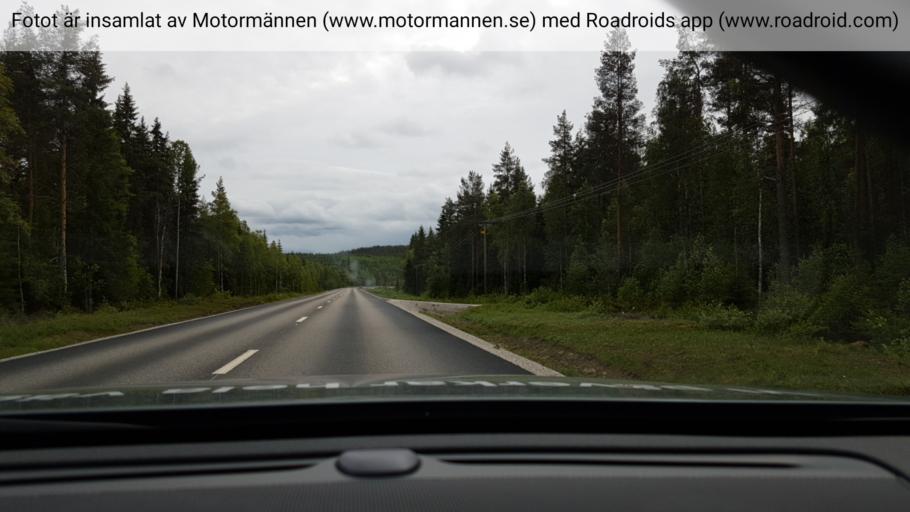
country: SE
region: Vaesterbotten
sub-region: Vindelns Kommun
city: Vindeln
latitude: 64.0477
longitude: 19.6801
